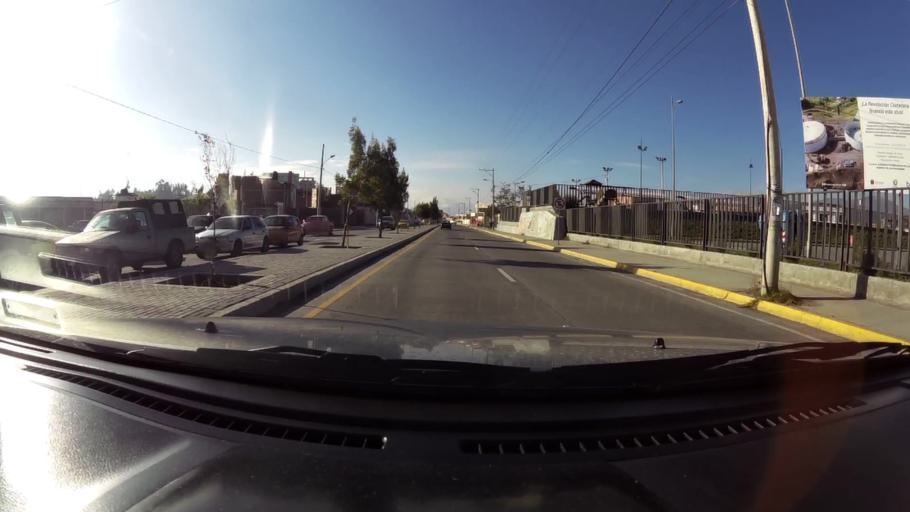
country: EC
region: Chimborazo
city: Riobamba
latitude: -1.6669
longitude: -78.6383
